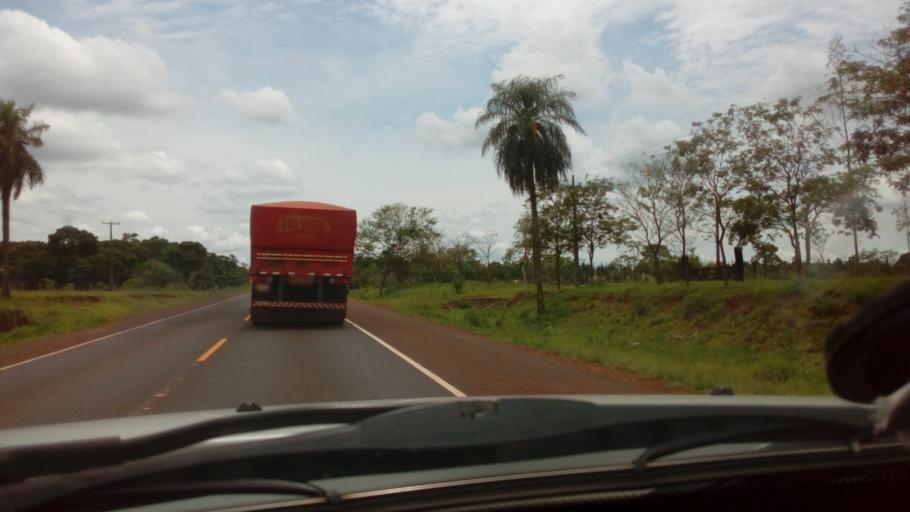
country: PY
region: Alto Parana
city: Colonia Yguazu
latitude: -25.5910
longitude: -54.9307
